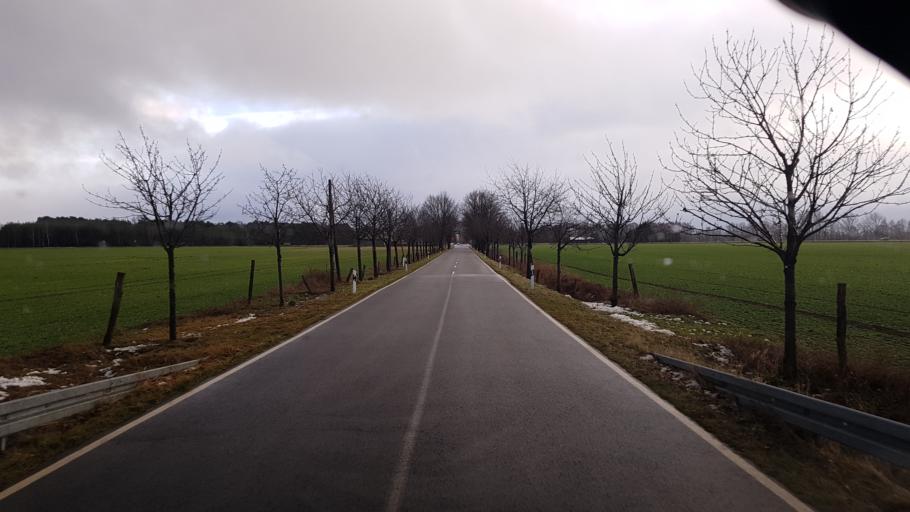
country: DE
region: Brandenburg
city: Heinersbruck
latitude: 51.8287
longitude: 14.5064
